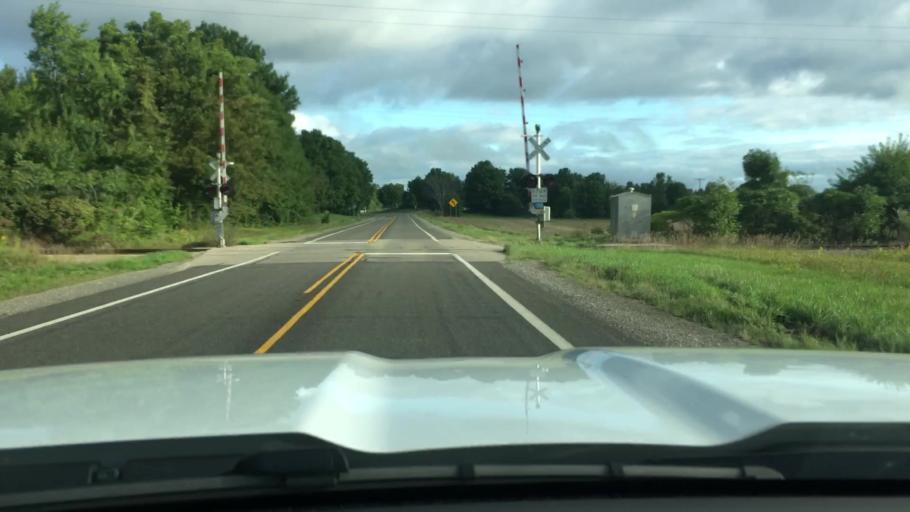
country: US
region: Michigan
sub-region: Lapeer County
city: Barnes Lake-Millers Lake
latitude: 43.3299
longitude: -83.3225
